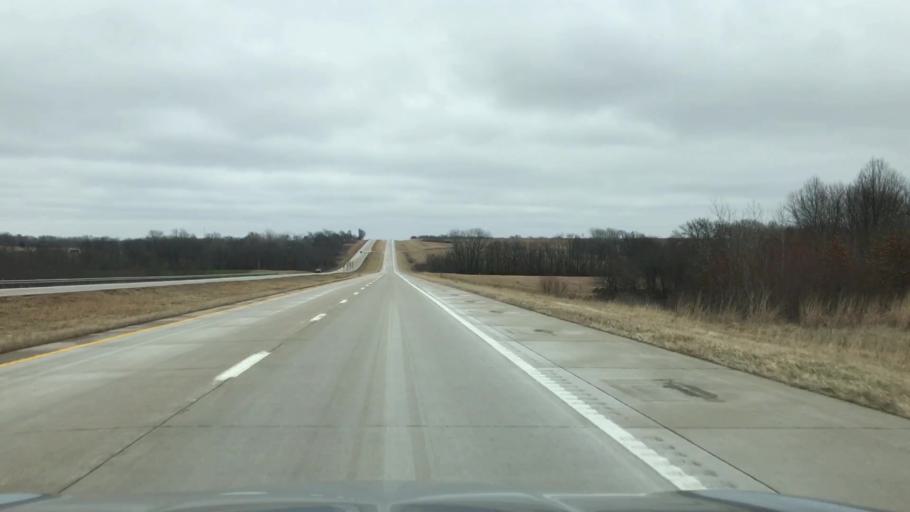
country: US
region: Missouri
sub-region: Livingston County
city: Chillicothe
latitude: 39.7377
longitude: -93.7047
